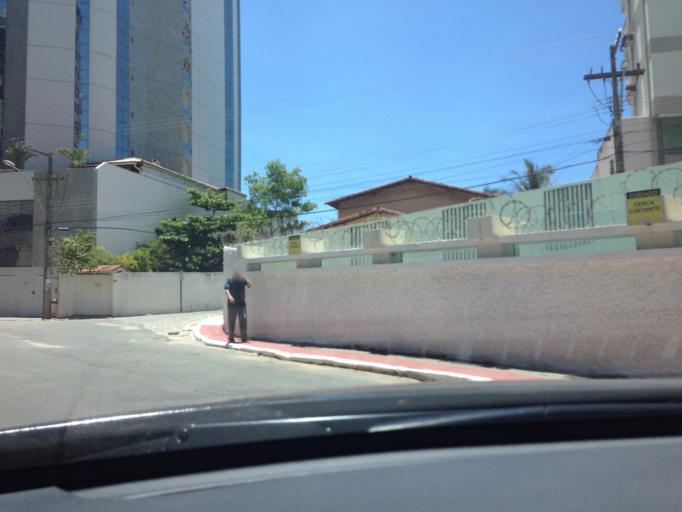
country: BR
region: Espirito Santo
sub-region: Guarapari
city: Guarapari
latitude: -20.6752
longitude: -40.5017
